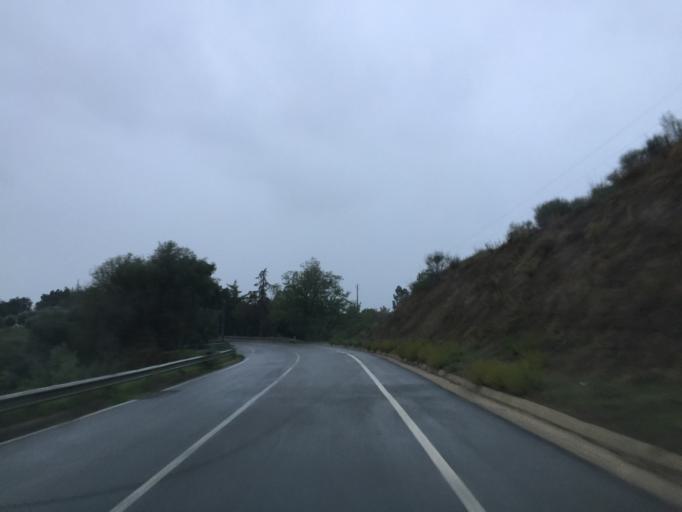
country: PT
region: Portalegre
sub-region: Avis
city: Avis
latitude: 39.0593
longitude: -7.8966
